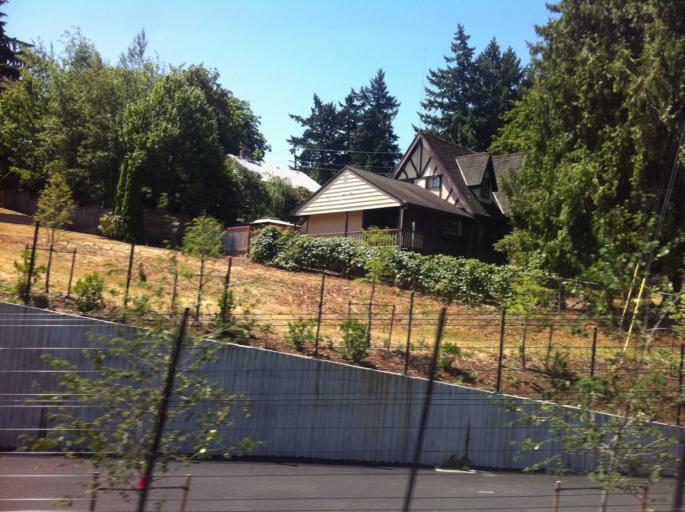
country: US
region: Oregon
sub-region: Clackamas County
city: Milwaukie
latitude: 45.4361
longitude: -122.6388
